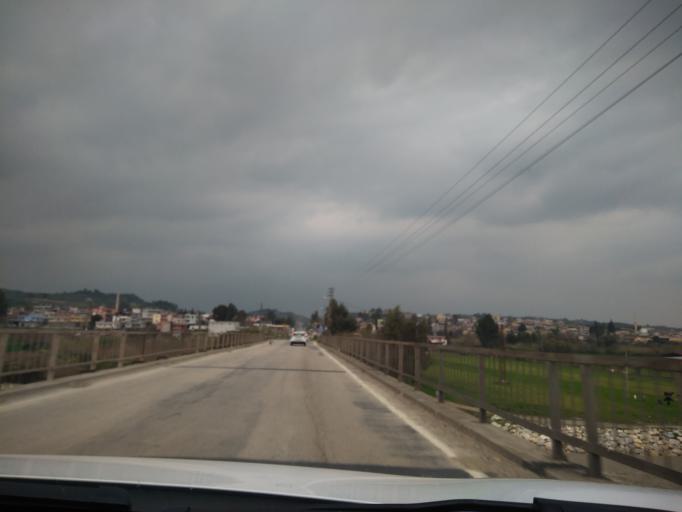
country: TR
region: Mersin
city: Yenice
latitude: 37.1027
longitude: 35.1097
